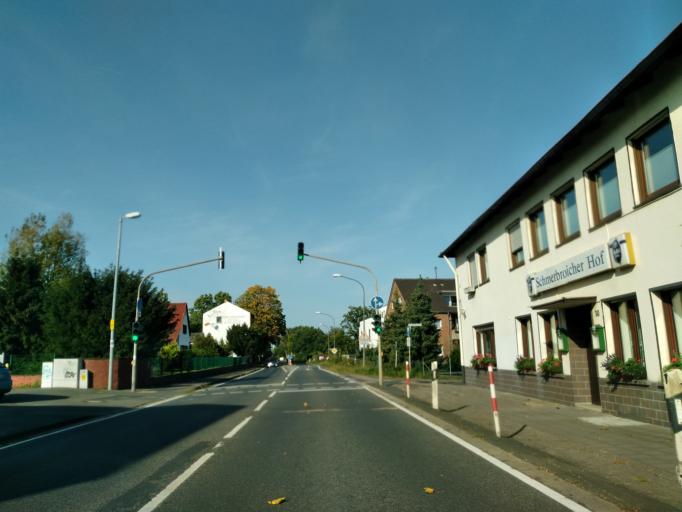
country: DE
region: North Rhine-Westphalia
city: Sankt Augustin
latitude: 50.7627
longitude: 7.2154
